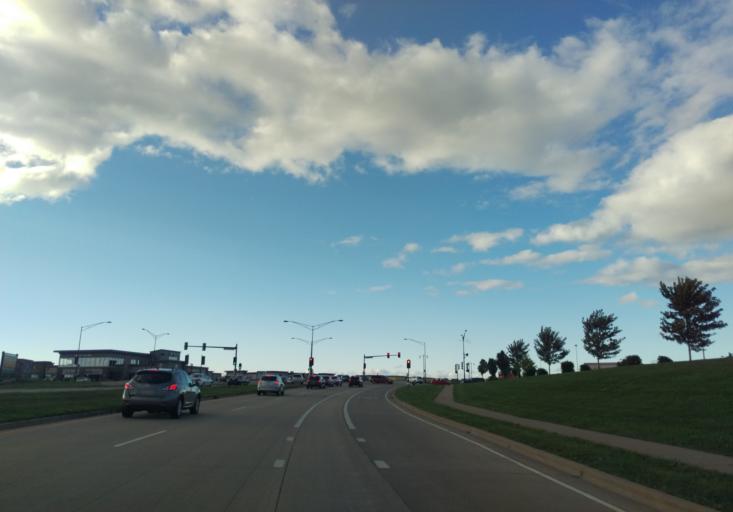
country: US
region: Wisconsin
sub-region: Dane County
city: Sun Prairie
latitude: 43.1649
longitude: -89.2689
